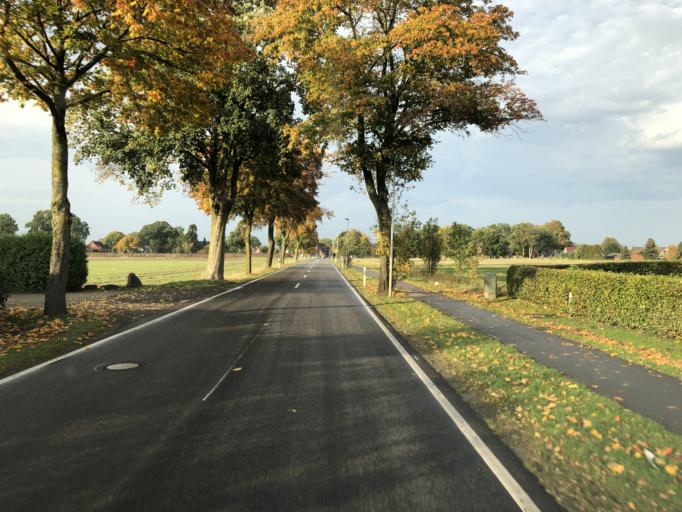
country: DE
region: Lower Saxony
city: Neu Wulmstorf
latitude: 53.4393
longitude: 9.8055
